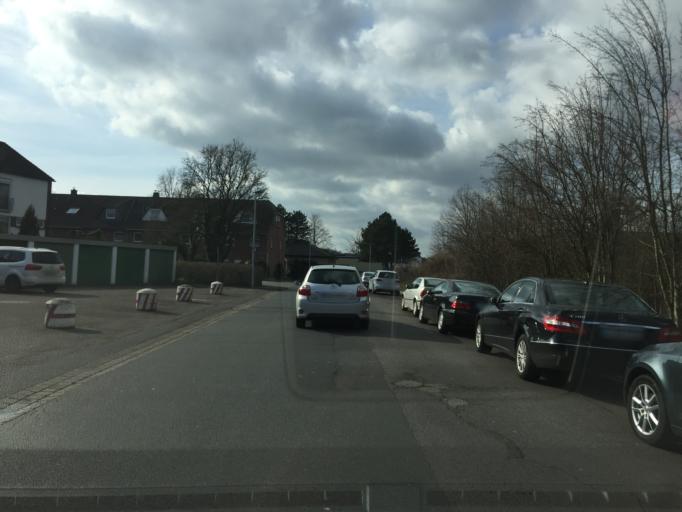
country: DE
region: Lower Saxony
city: Garbsen
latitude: 52.4220
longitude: 9.5808
